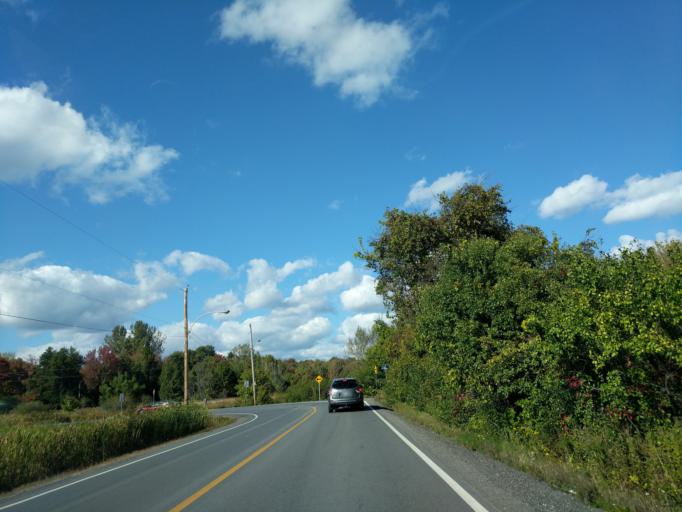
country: CA
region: Ontario
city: Ottawa
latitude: 45.4136
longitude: -75.7843
